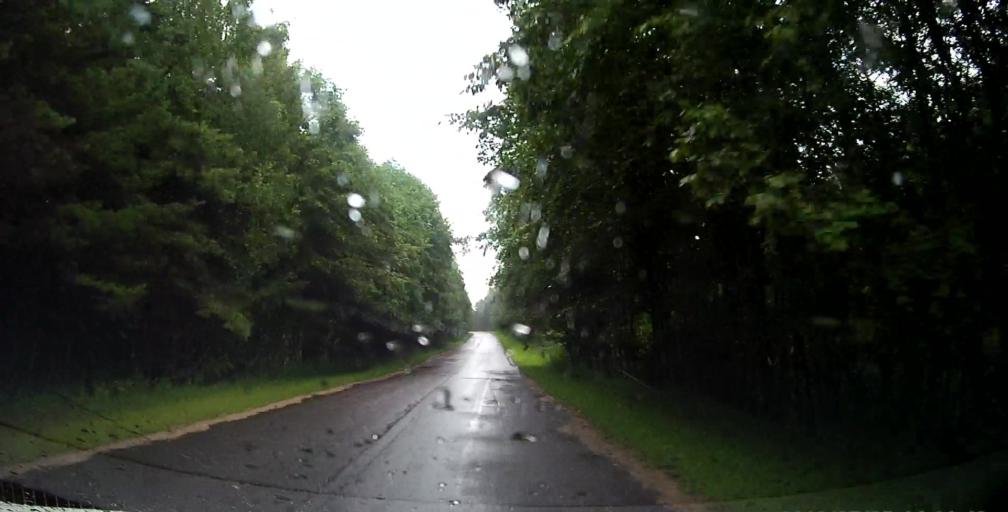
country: RU
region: Smolensk
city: Demidov
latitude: 55.4591
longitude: 31.6096
